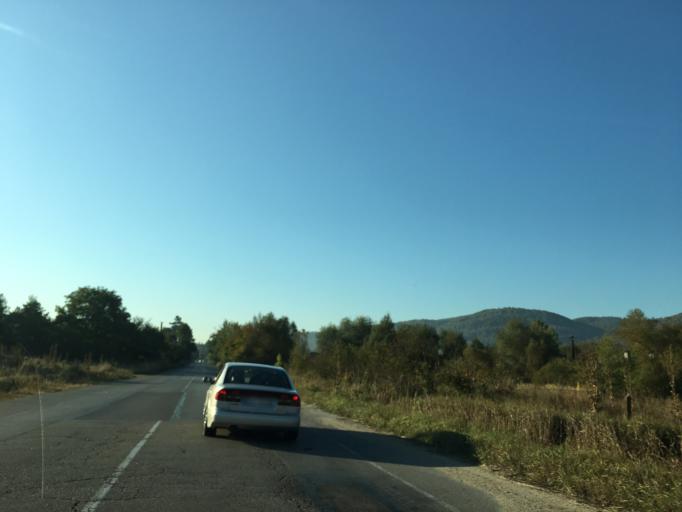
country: BG
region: Sofiya
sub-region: Obshtina Ikhtiman
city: Ikhtiman
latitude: 42.3933
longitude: 23.8703
